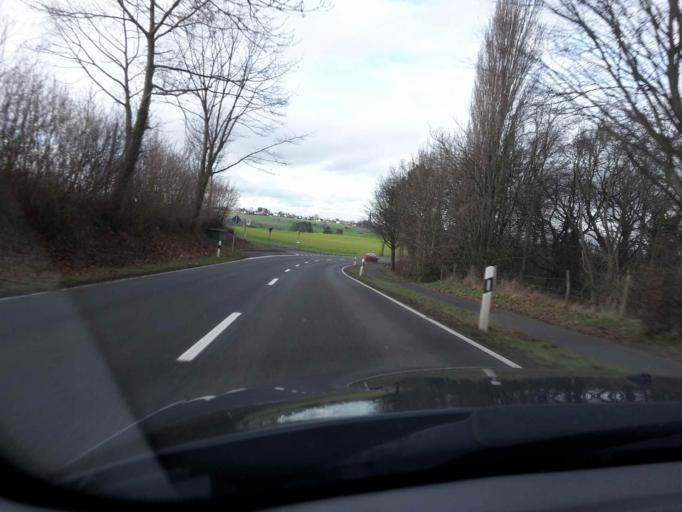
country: DE
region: North Rhine-Westphalia
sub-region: Regierungsbezirk Koln
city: Hennef
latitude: 50.7376
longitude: 7.2878
